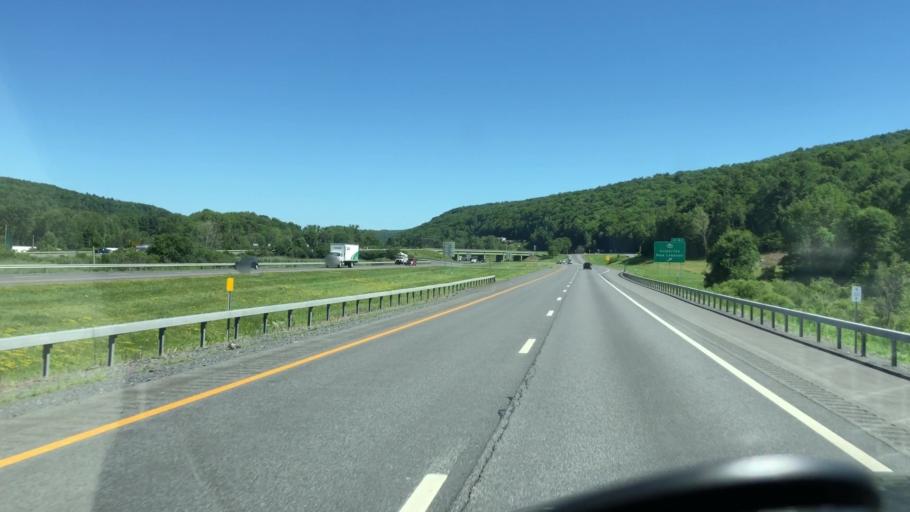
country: US
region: Massachusetts
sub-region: Berkshire County
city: Richmond
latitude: 42.3620
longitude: -73.4315
